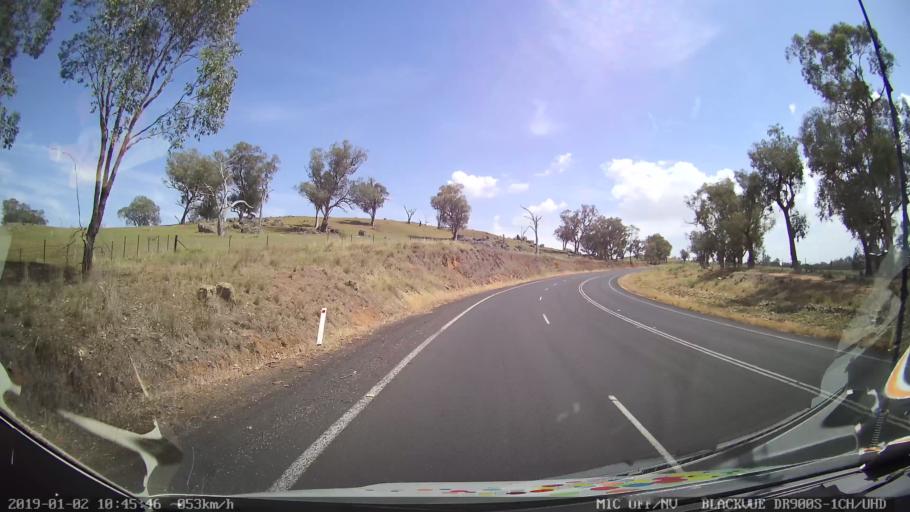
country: AU
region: New South Wales
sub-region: Cootamundra
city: Cootamundra
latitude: -34.7571
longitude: 148.2889
